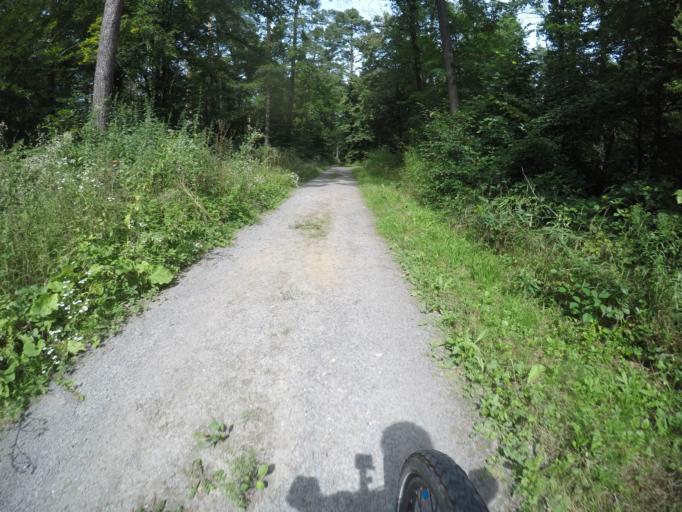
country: DE
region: Baden-Wuerttemberg
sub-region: Karlsruhe Region
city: Hambrucken
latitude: 49.2056
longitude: 8.5483
